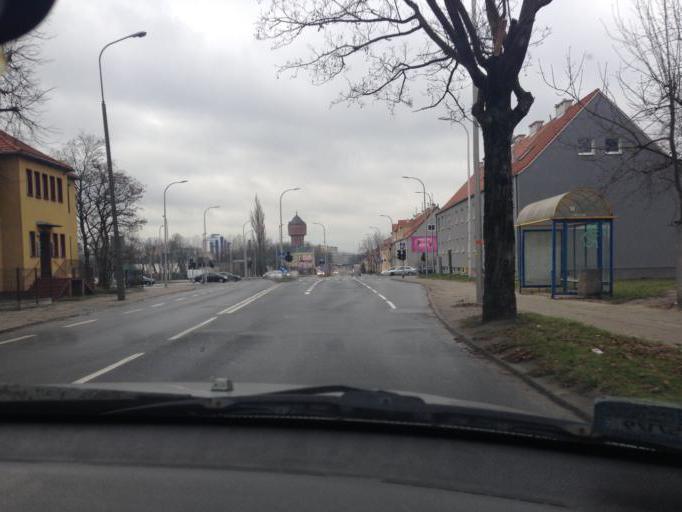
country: PL
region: Opole Voivodeship
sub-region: Powiat opolski
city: Opole
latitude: 50.6794
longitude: 17.9379
